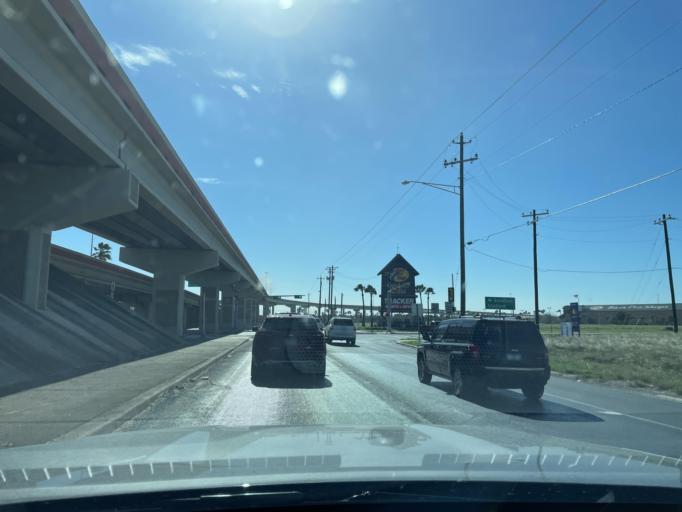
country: US
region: Texas
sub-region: Cameron County
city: Harlingen
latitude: 26.1960
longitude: -97.7203
